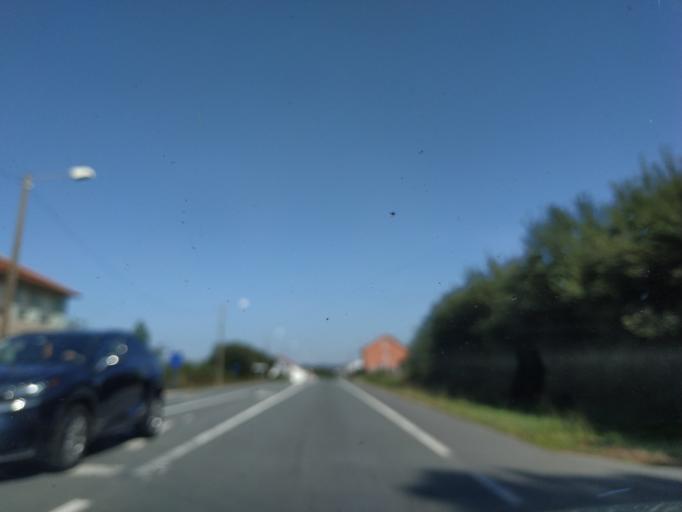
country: ES
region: Galicia
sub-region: Provincia da Coruna
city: Laracha
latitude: 43.2469
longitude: -8.6230
